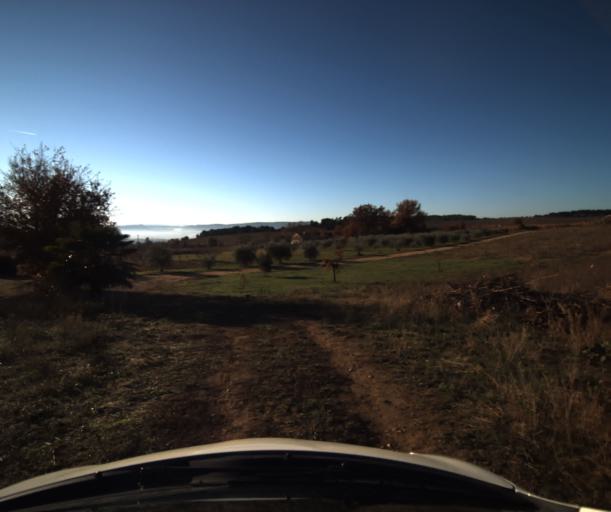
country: FR
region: Provence-Alpes-Cote d'Azur
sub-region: Departement du Vaucluse
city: Pertuis
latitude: 43.7230
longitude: 5.4944
